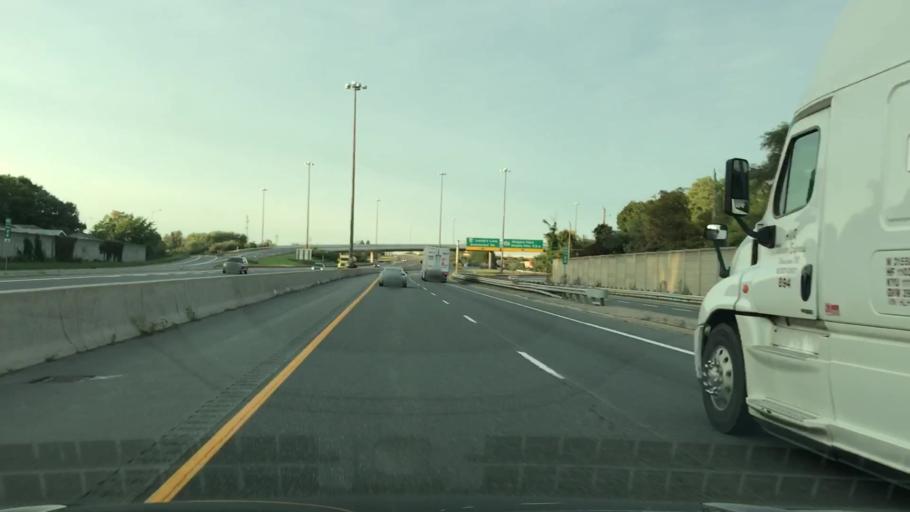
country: CA
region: Ontario
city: Niagara Falls
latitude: 43.0929
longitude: -79.1190
